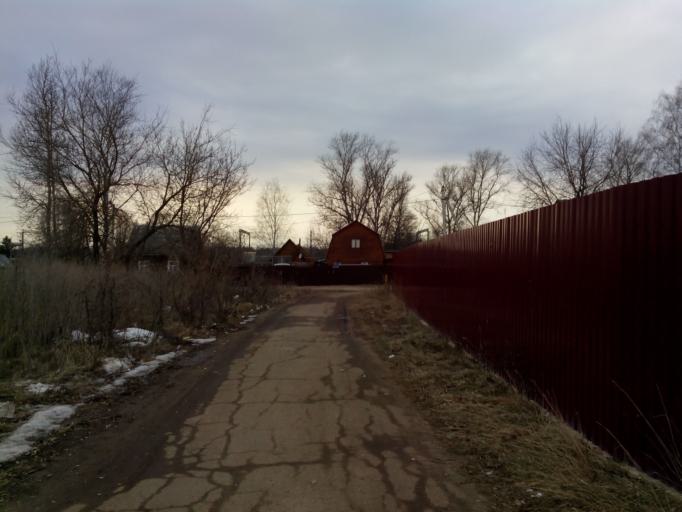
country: RU
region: Moskovskaya
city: Orud'yevo
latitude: 56.4444
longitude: 37.5214
